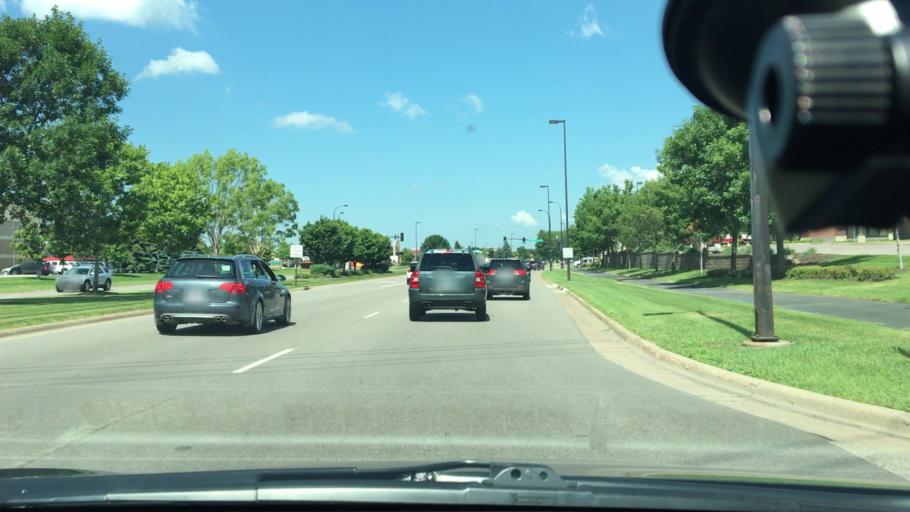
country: US
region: Minnesota
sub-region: Hennepin County
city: Maple Grove
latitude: 45.0962
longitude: -93.4460
